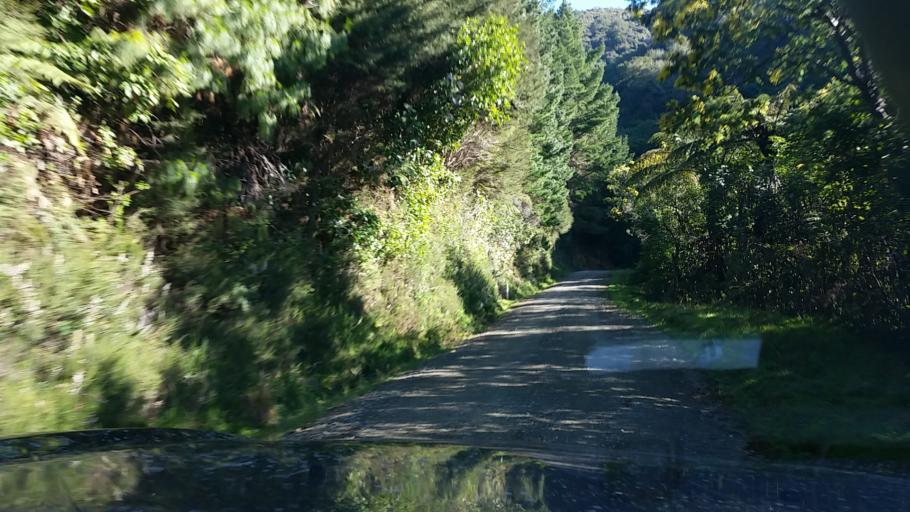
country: NZ
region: Marlborough
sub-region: Marlborough District
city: Picton
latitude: -41.1426
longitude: 174.0480
